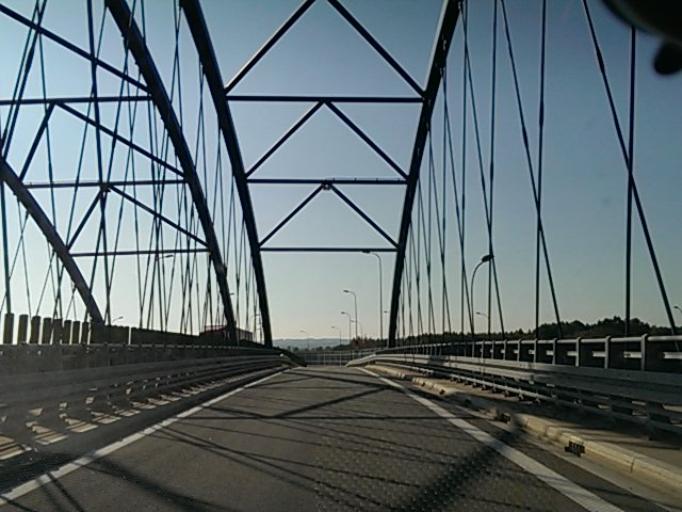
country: PL
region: Subcarpathian Voivodeship
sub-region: Powiat ropczycko-sedziszowski
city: Sedziszow Malopolski
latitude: 50.1087
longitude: 21.6650
